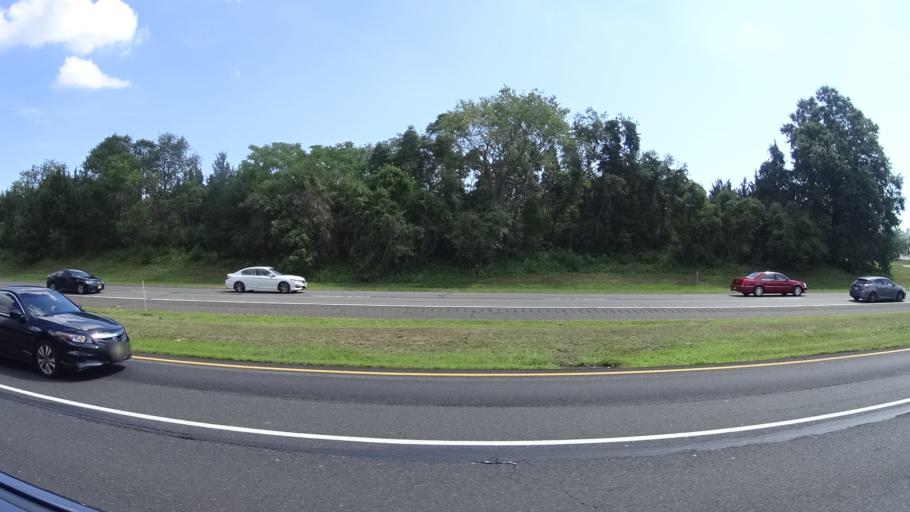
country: US
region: New Jersey
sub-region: Monmouth County
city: Tinton Falls
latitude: 40.2982
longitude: -74.0930
